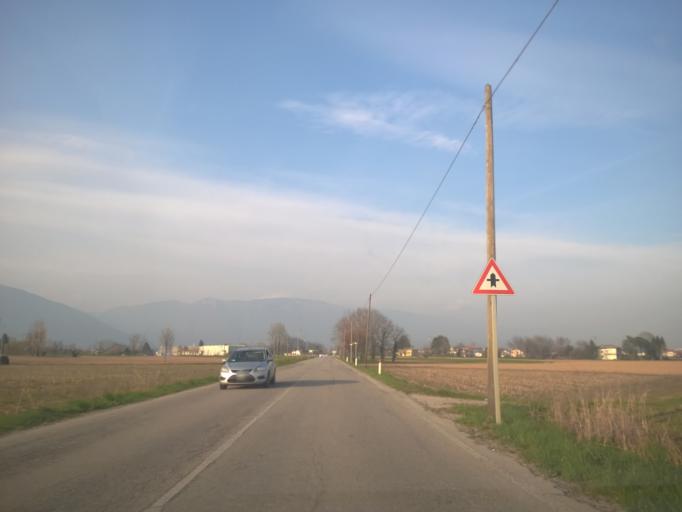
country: IT
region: Veneto
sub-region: Provincia di Vicenza
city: Giavenale
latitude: 45.6878
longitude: 11.4129
